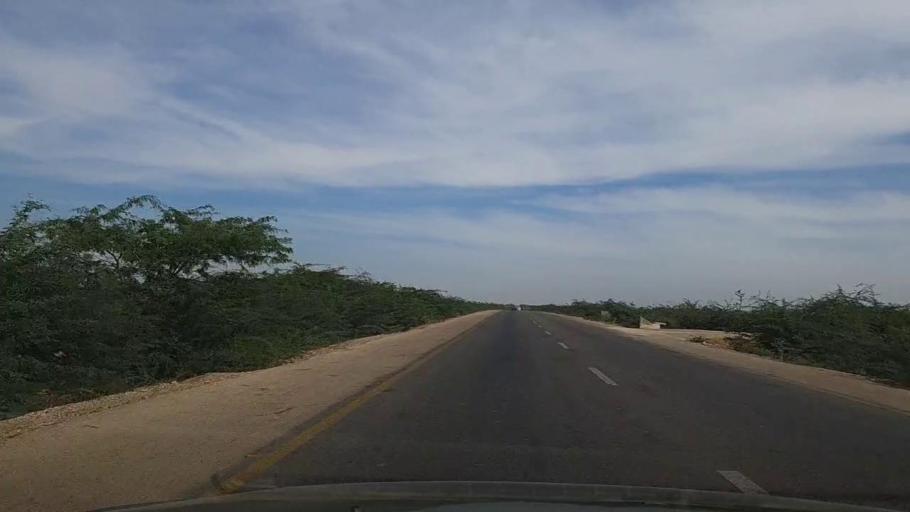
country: PK
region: Sindh
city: Thatta
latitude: 24.8416
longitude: 68.0065
